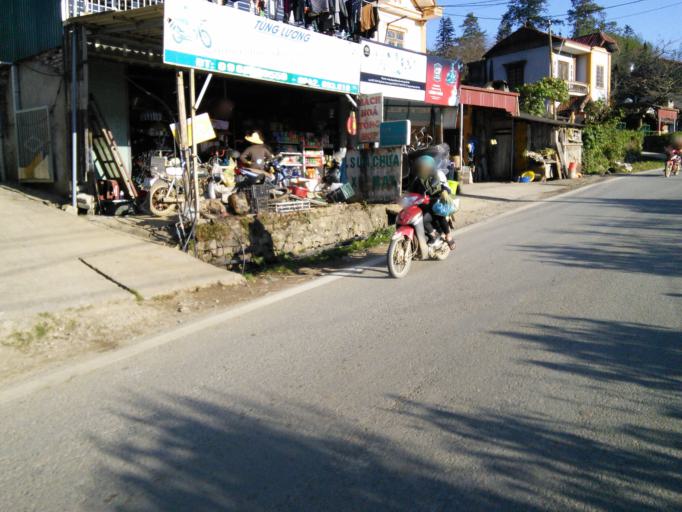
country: VN
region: Lao Cai
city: Sa Pa
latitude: 22.3682
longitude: 103.8024
